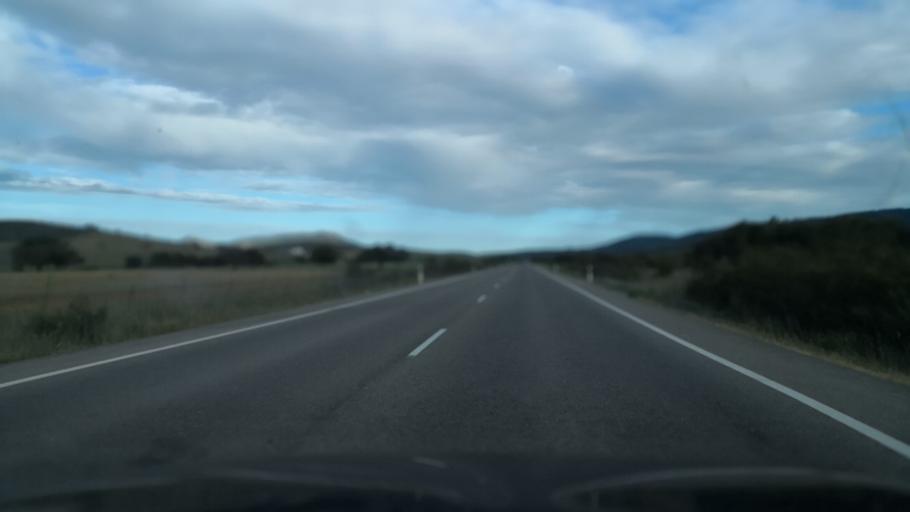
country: ES
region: Extremadura
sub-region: Provincia de Caceres
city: Pedroso de Acim
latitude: 39.8572
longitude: -6.4248
